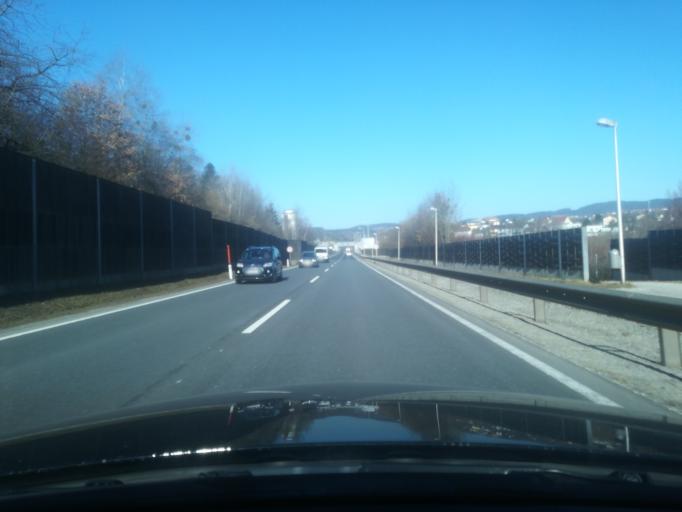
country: AT
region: Upper Austria
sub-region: Politischer Bezirk Urfahr-Umgebung
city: Engerwitzdorf
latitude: 48.3516
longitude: 14.5231
